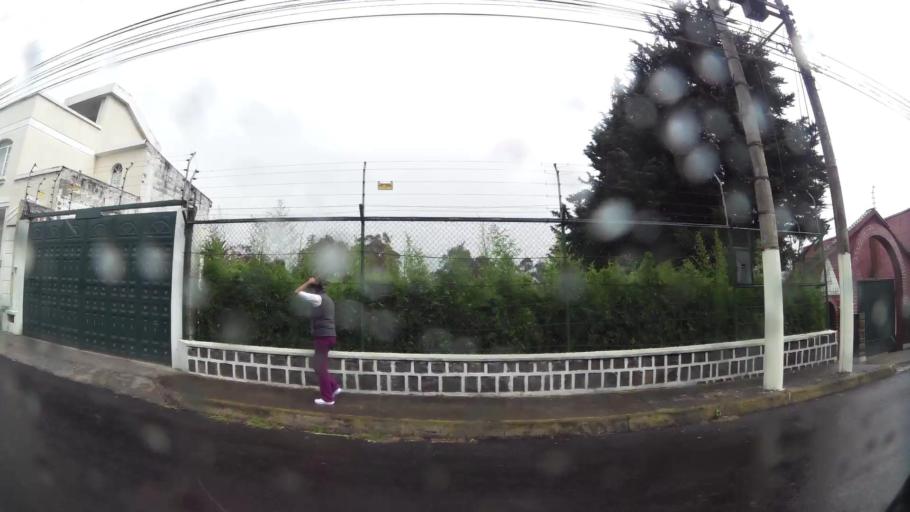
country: EC
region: Pichincha
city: Sangolqui
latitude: -0.2892
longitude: -78.4761
